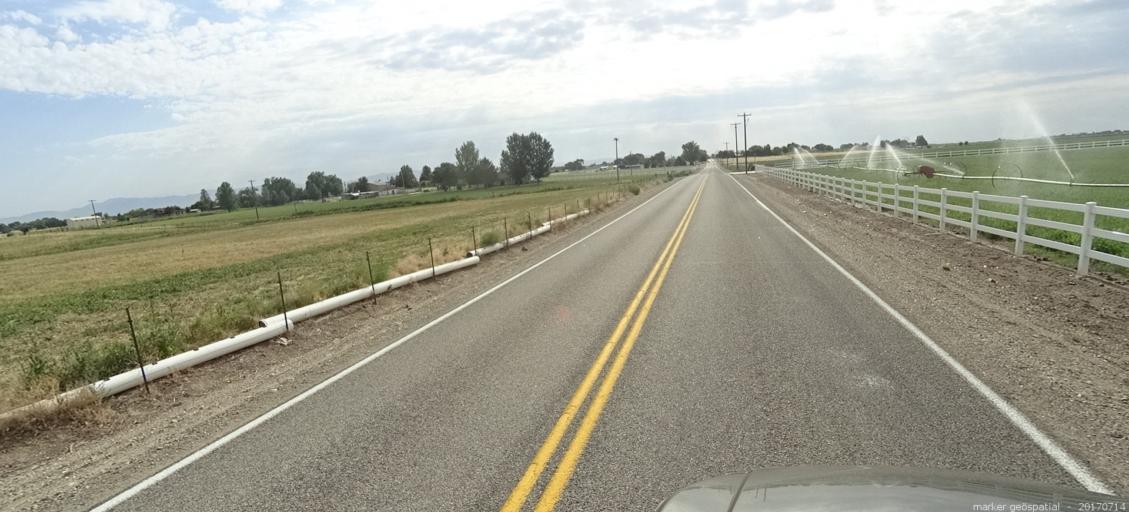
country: US
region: Idaho
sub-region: Ada County
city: Kuna
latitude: 43.4737
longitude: -116.3659
